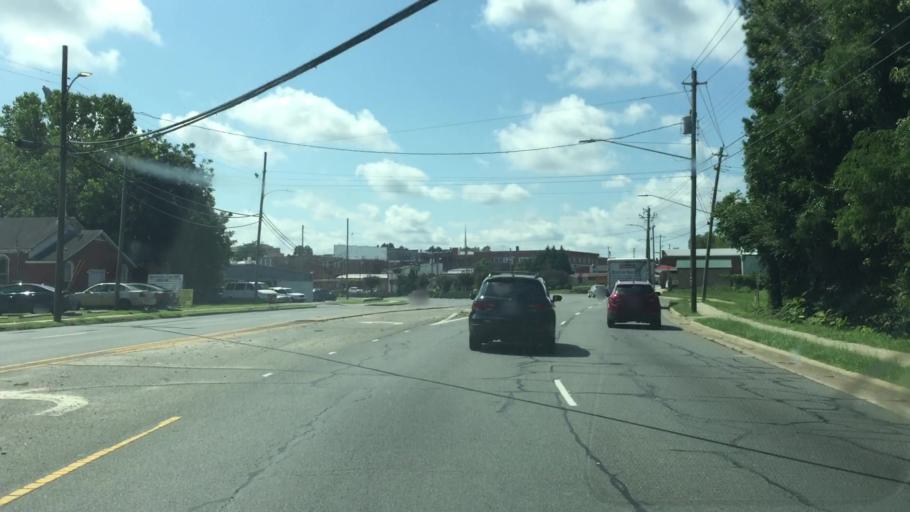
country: US
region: North Carolina
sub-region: Anson County
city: Wadesboro
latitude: 34.9700
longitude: -80.0791
